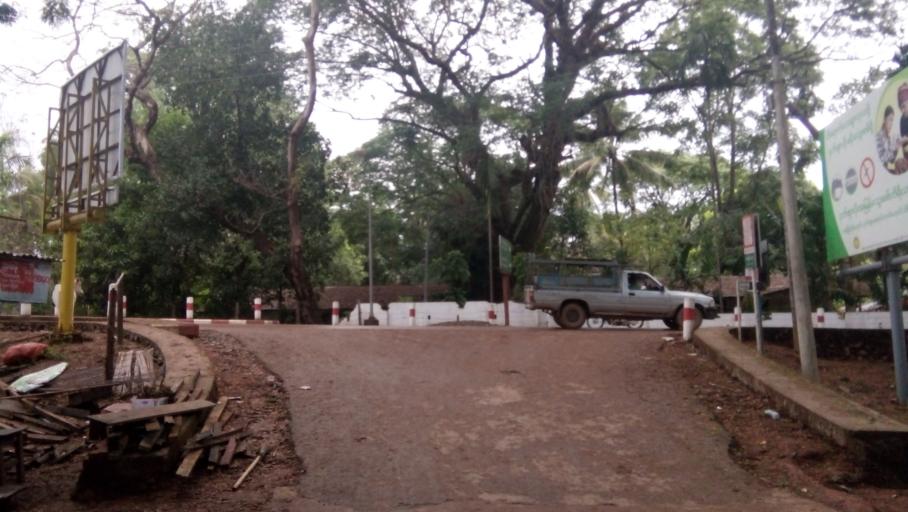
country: MM
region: Kayin
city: Hpa-an
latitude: 17.1205
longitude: 97.8178
